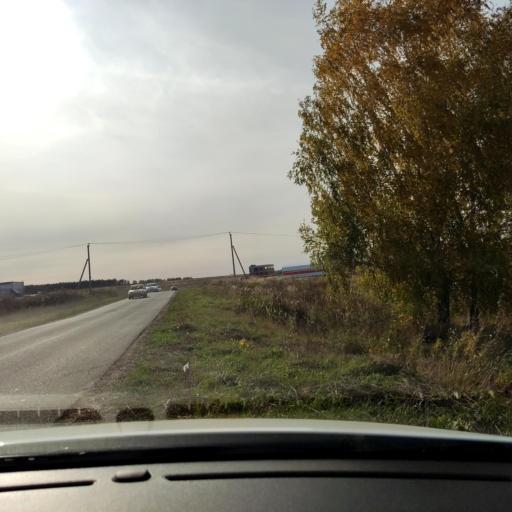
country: RU
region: Tatarstan
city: Vysokaya Gora
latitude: 55.8543
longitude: 49.3430
